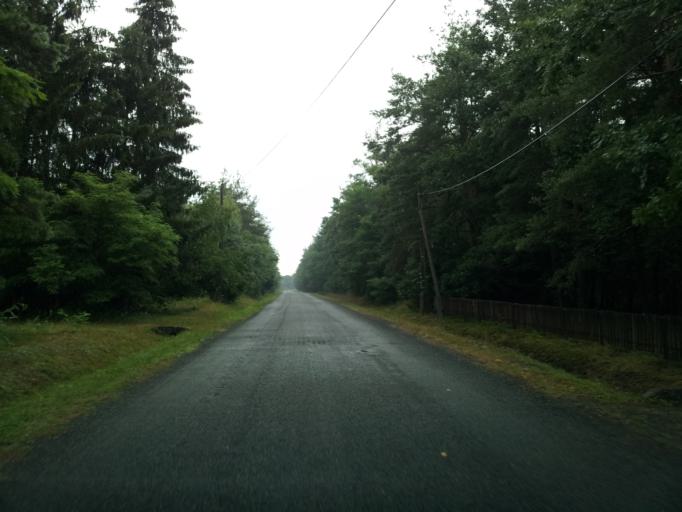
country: HU
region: Zala
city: Zalalovo
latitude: 46.8798
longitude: 16.5487
